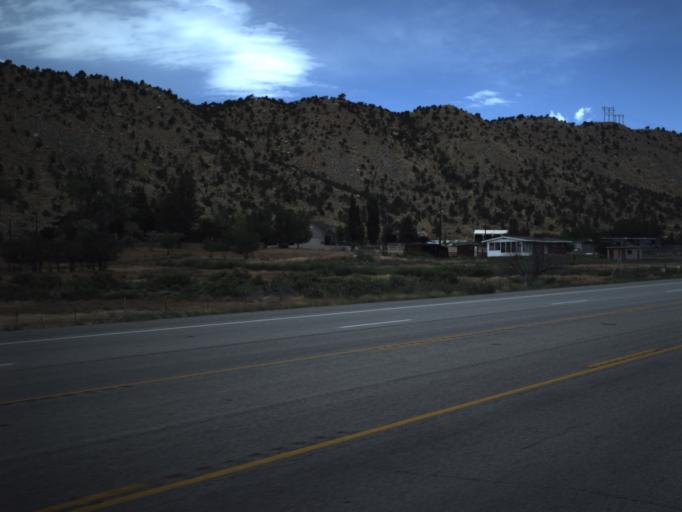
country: US
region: Utah
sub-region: Carbon County
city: Helper
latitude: 39.6740
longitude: -110.8616
